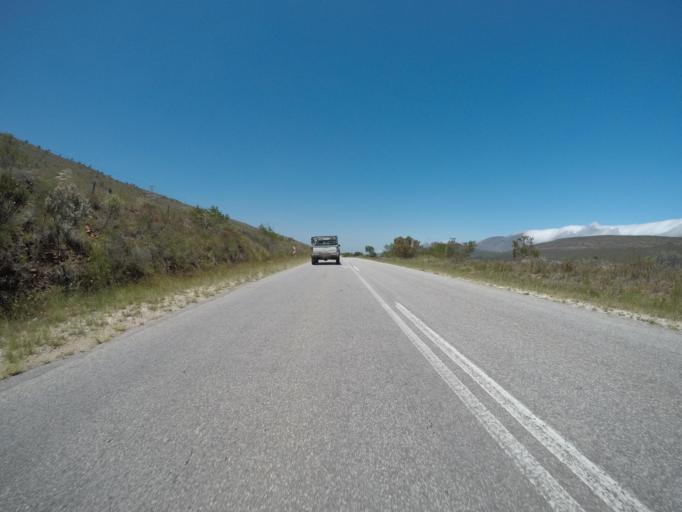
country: ZA
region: Eastern Cape
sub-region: Cacadu District Municipality
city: Kareedouw
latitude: -33.8399
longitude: 23.9301
